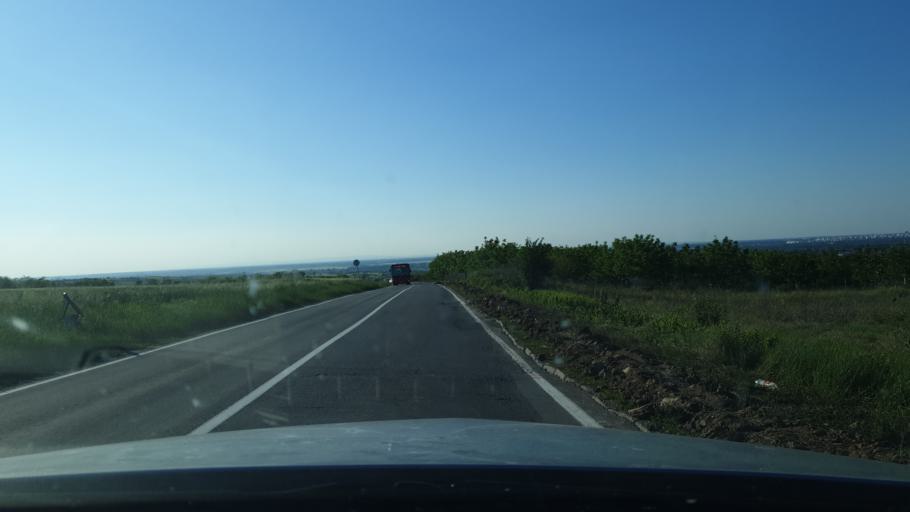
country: RS
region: Central Serbia
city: Sremcica
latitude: 44.7005
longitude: 20.3770
